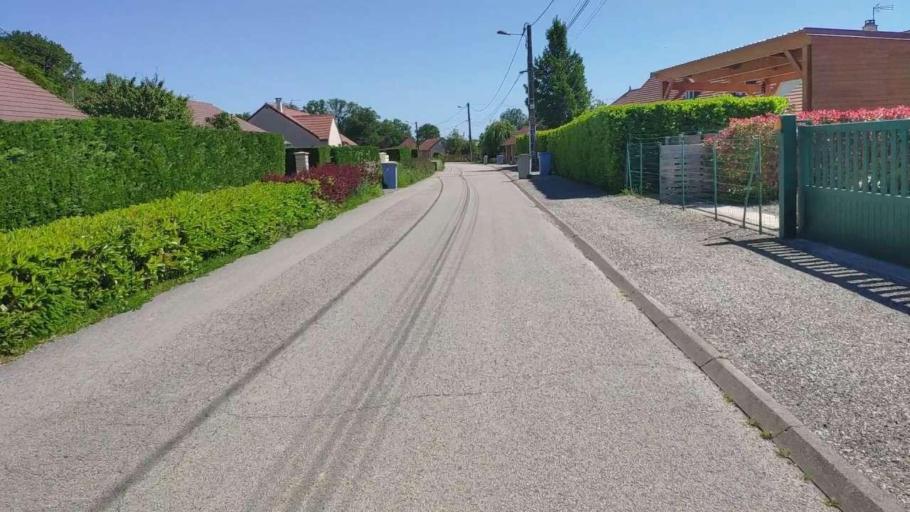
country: FR
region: Franche-Comte
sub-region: Departement du Jura
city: Bletterans
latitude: 46.7629
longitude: 5.4433
